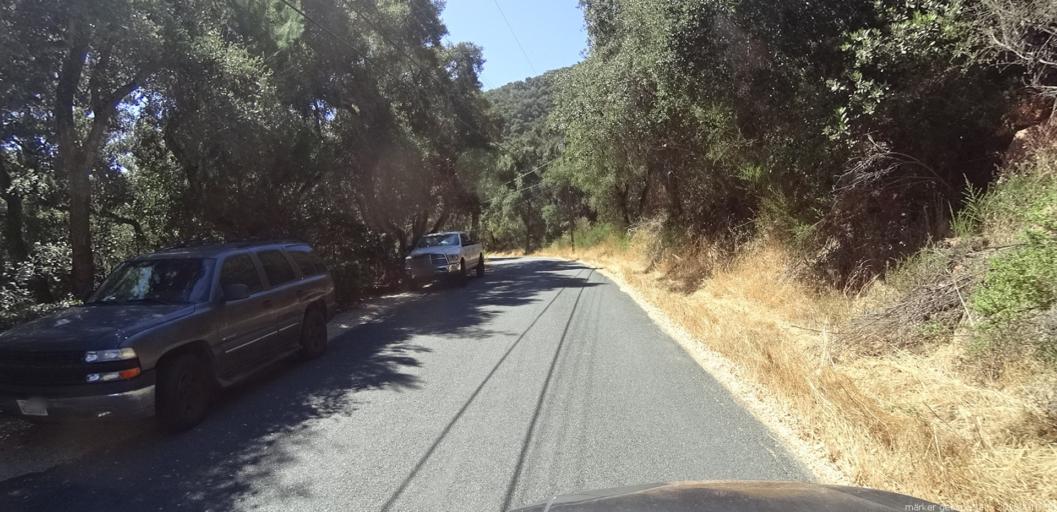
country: US
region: California
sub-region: Monterey County
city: Carmel Valley Village
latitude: 36.5167
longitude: -121.8127
